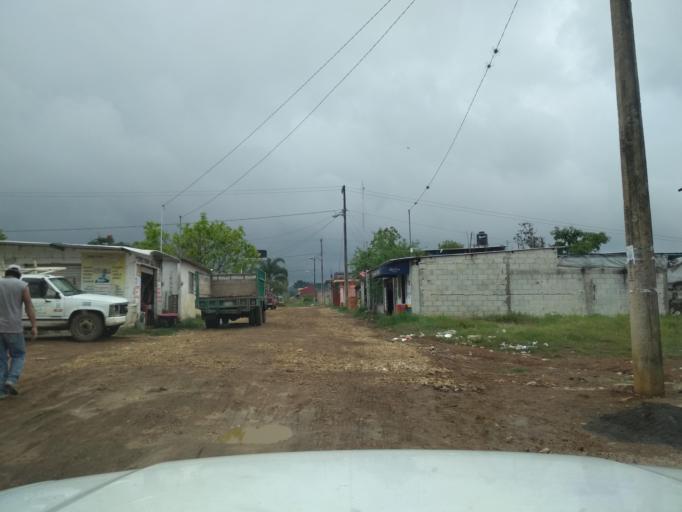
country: MX
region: Veracruz
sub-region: Cordoba
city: San Jose de Tapia
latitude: 18.8450
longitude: -96.9659
